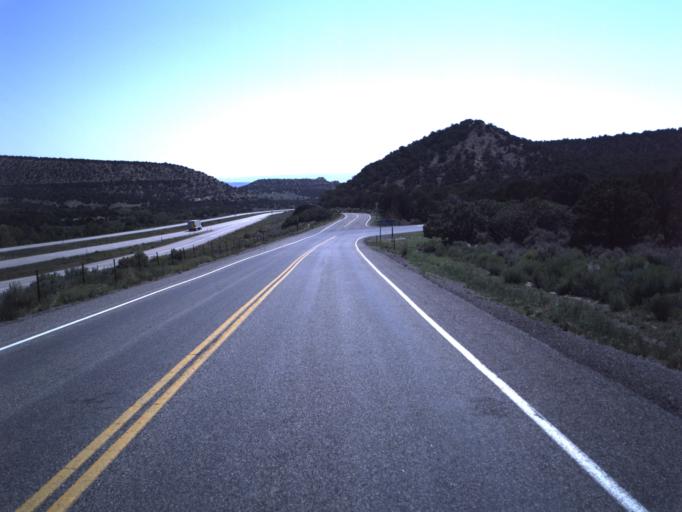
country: US
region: Utah
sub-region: Wayne County
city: Loa
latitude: 38.7563
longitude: -111.4222
